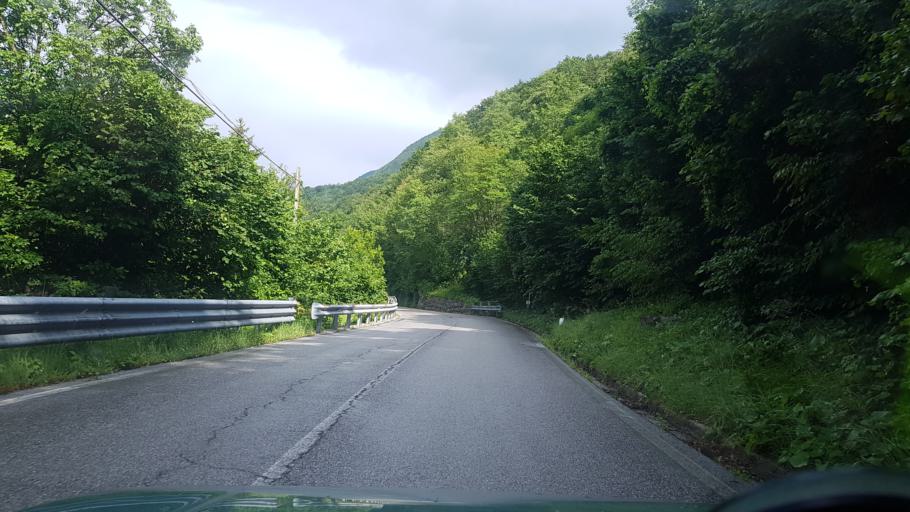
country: IT
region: Friuli Venezia Giulia
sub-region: Provincia di Udine
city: Lusevera
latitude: 46.3051
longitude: 13.2911
